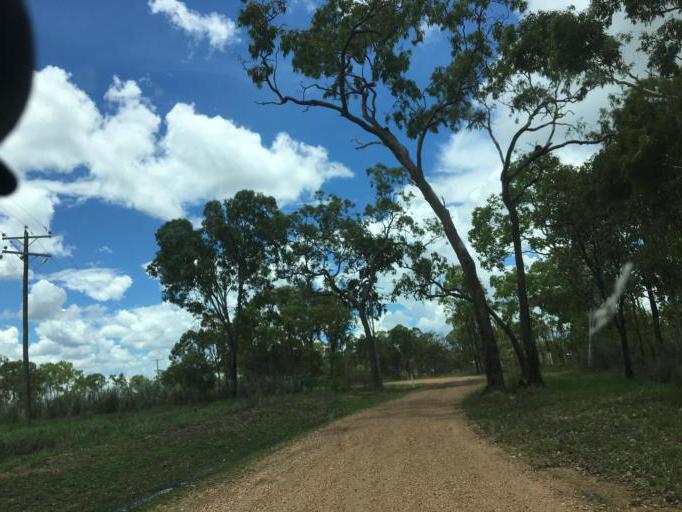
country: AU
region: Queensland
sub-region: Tablelands
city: Mareeba
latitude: -16.9927
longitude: 145.5212
